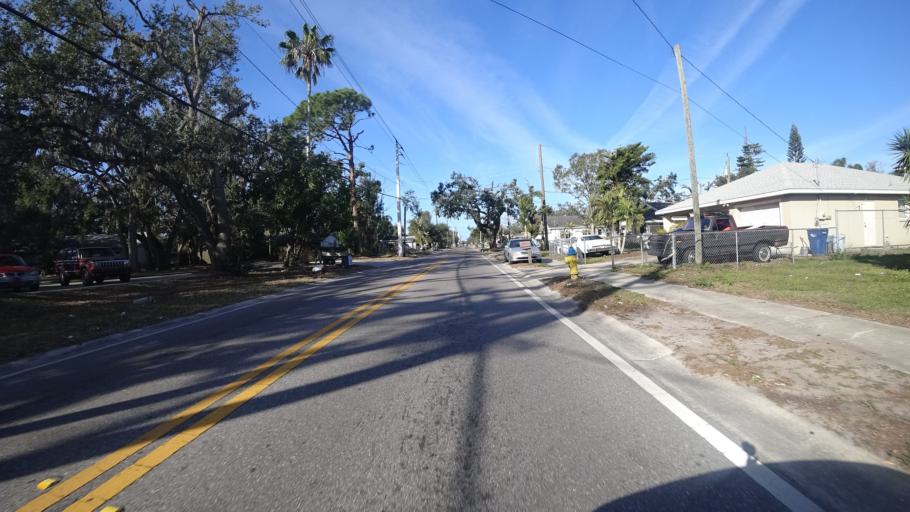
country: US
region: Florida
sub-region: Manatee County
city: West Samoset
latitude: 27.4770
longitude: -82.5563
